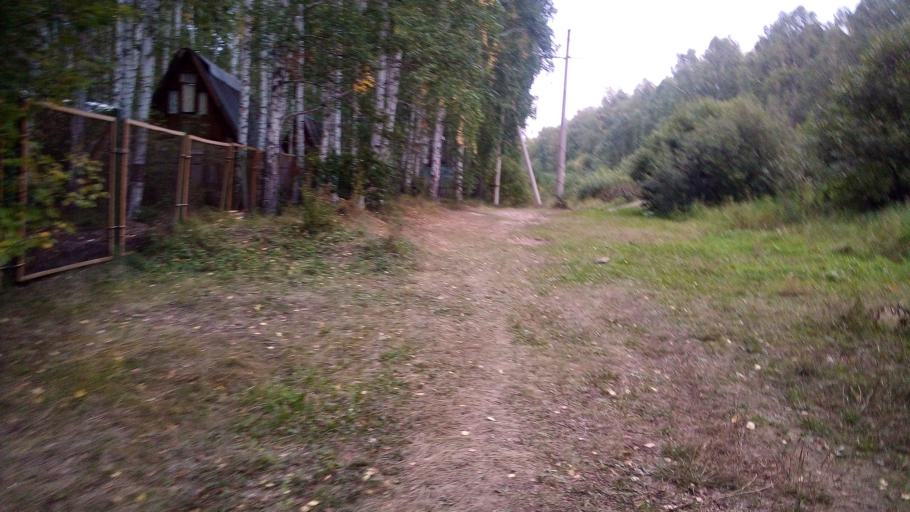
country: RU
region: Chelyabinsk
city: Tayginka
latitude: 55.4759
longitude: 60.4969
